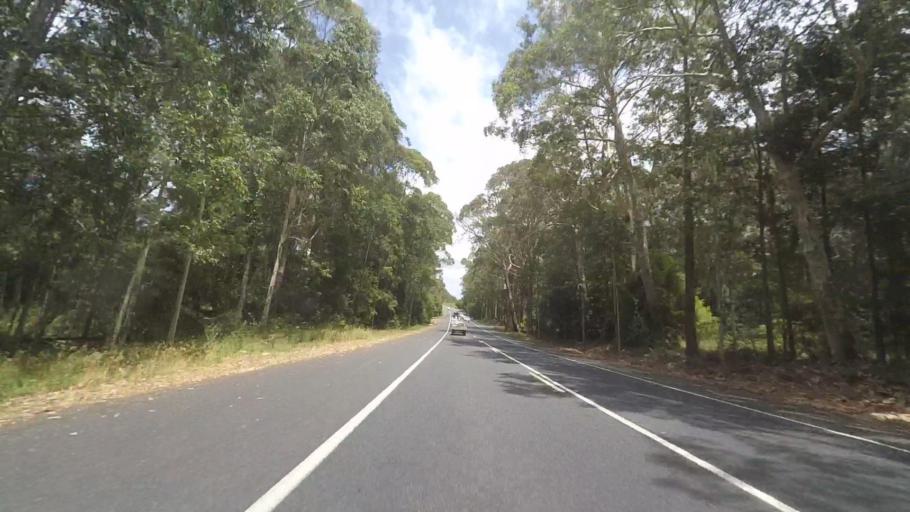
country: AU
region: New South Wales
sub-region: Shoalhaven Shire
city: Falls Creek
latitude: -35.0804
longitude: 150.5480
